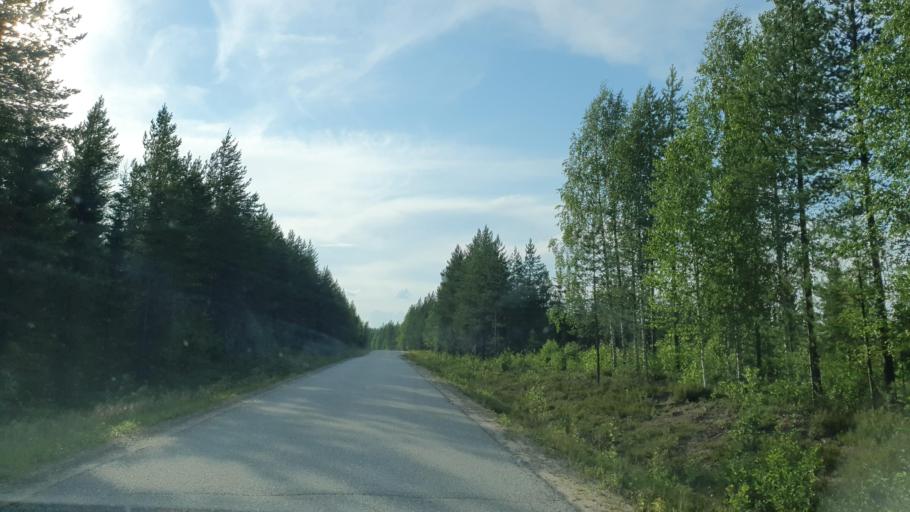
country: FI
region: Kainuu
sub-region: Kehys-Kainuu
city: Kuhmo
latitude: 64.2775
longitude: 29.4311
